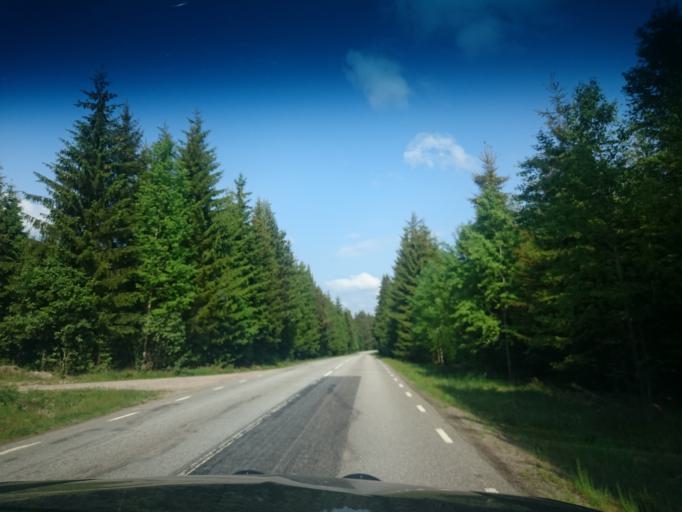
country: SE
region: Joenkoeping
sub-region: Vetlanda Kommun
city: Vetlanda
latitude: 57.3807
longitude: 15.0072
